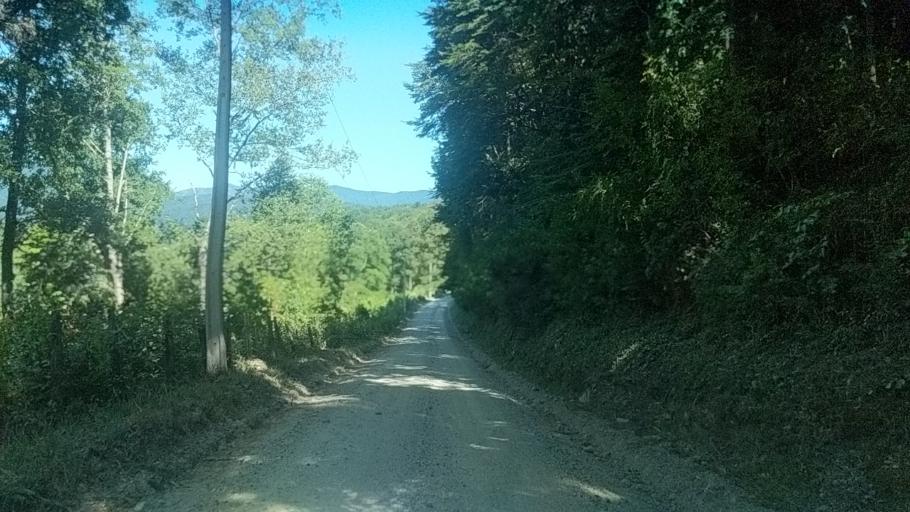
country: CL
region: Araucania
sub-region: Provincia de Cautin
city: Pucon
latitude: -39.0645
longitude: -71.7405
